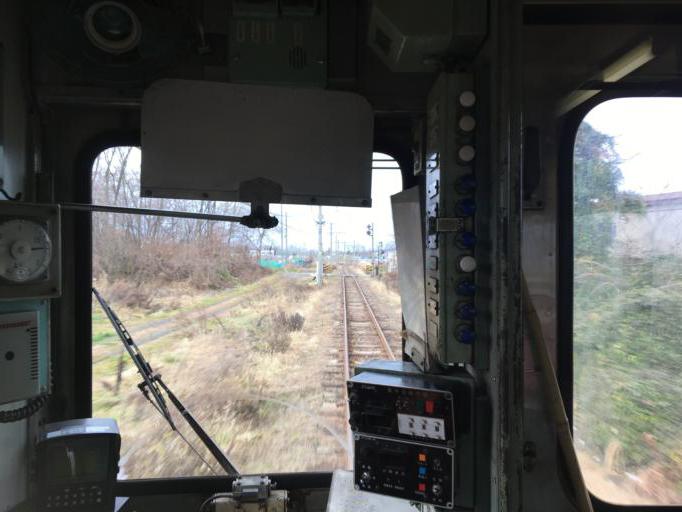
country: JP
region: Aomori
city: Hirosaki
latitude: 40.5616
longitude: 140.4937
